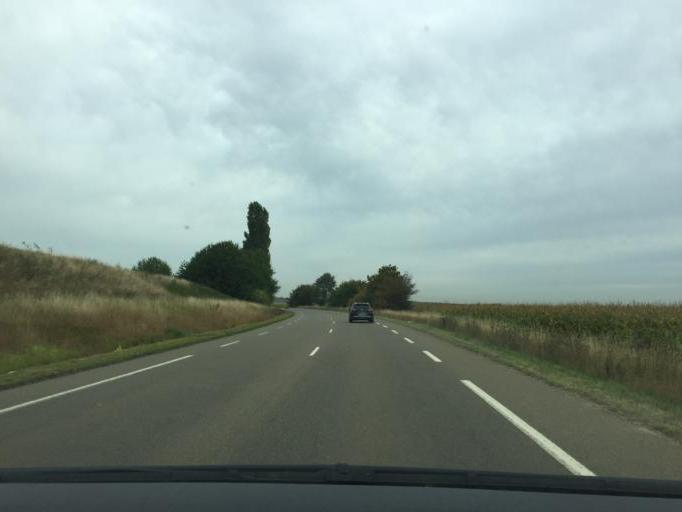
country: FR
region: Ile-de-France
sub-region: Departement de l'Essonne
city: Villiers-le-Bacle
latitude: 48.7446
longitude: 2.1220
